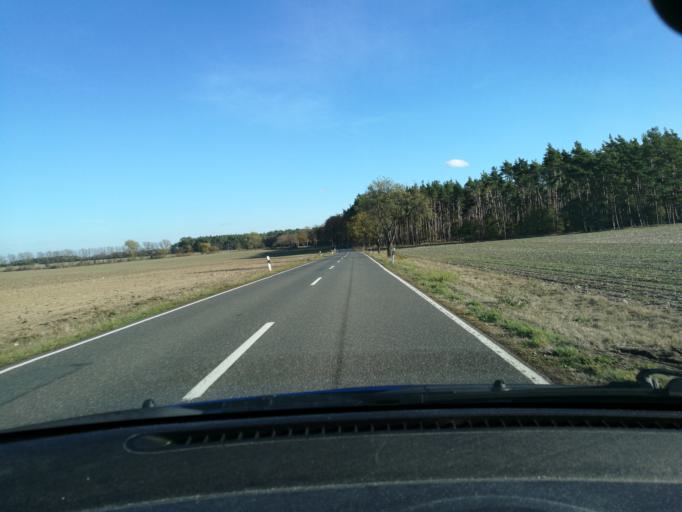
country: DE
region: Brandenburg
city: Karstadt
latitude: 53.1648
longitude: 11.6493
